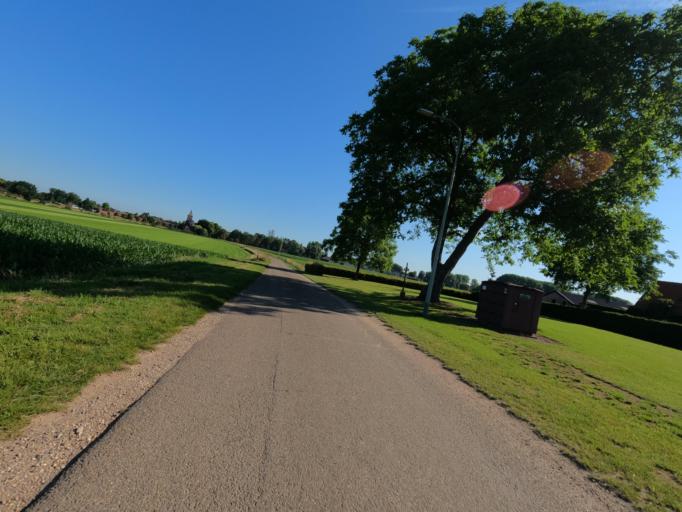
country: NL
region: Limburg
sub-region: Gemeente Roerdalen
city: Vlodrop
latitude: 51.1261
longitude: 6.0773
